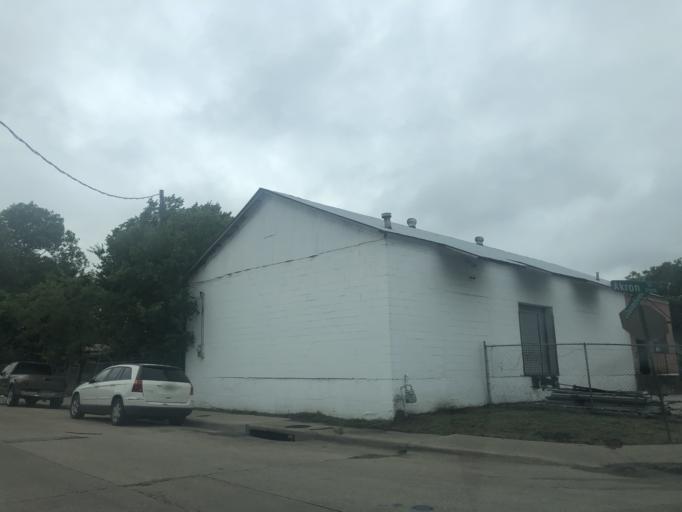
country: US
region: Texas
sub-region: Dallas County
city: Cockrell Hill
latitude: 32.7768
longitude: -96.8576
